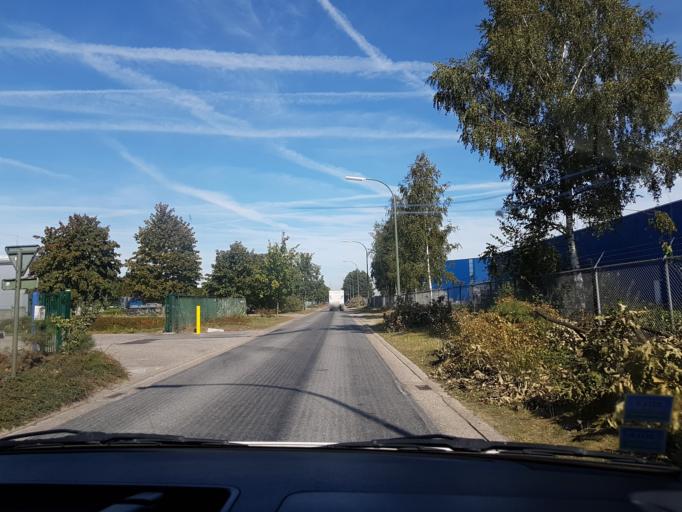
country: BE
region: Flanders
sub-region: Provincie Limburg
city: Overpelt
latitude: 51.2178
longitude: 5.3836
